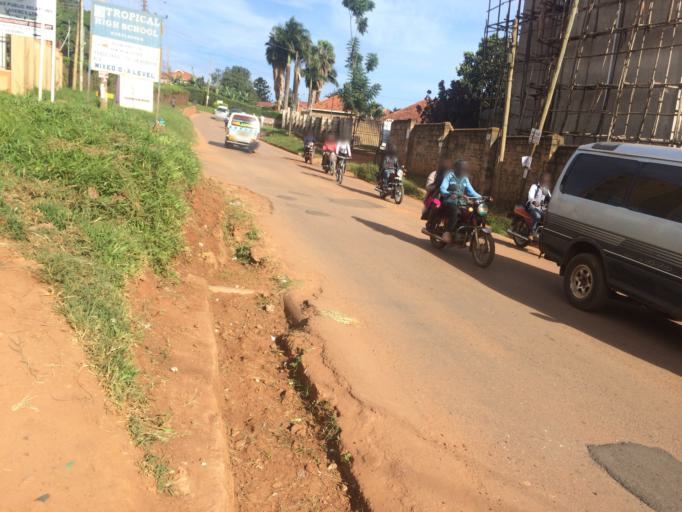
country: UG
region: Central Region
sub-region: Kampala District
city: Kampala
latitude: 0.2975
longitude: 32.5953
